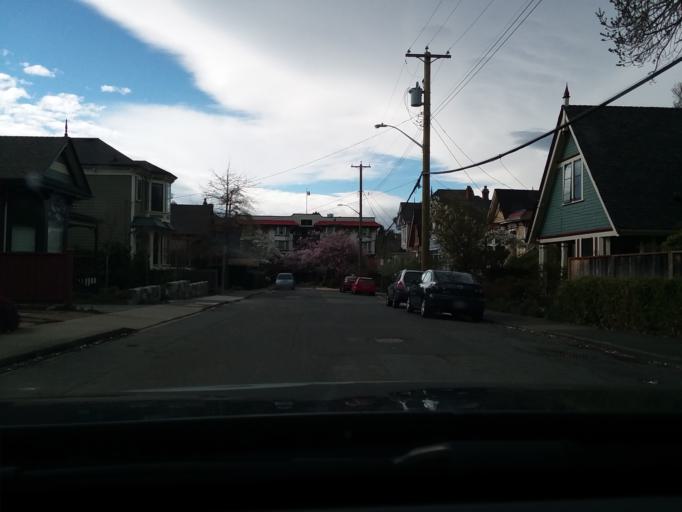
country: CA
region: British Columbia
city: Victoria
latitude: 48.4150
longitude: -123.3679
